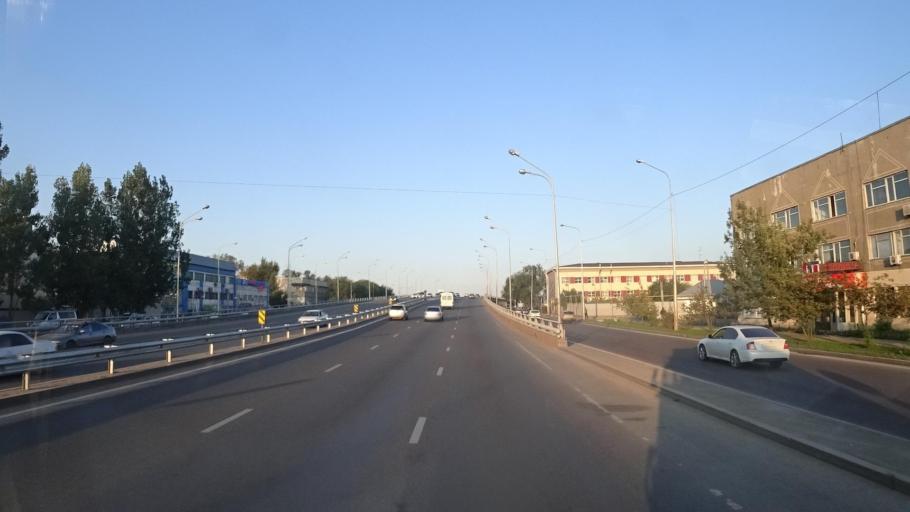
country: KZ
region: Almaty Qalasy
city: Almaty
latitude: 43.2917
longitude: 76.9318
